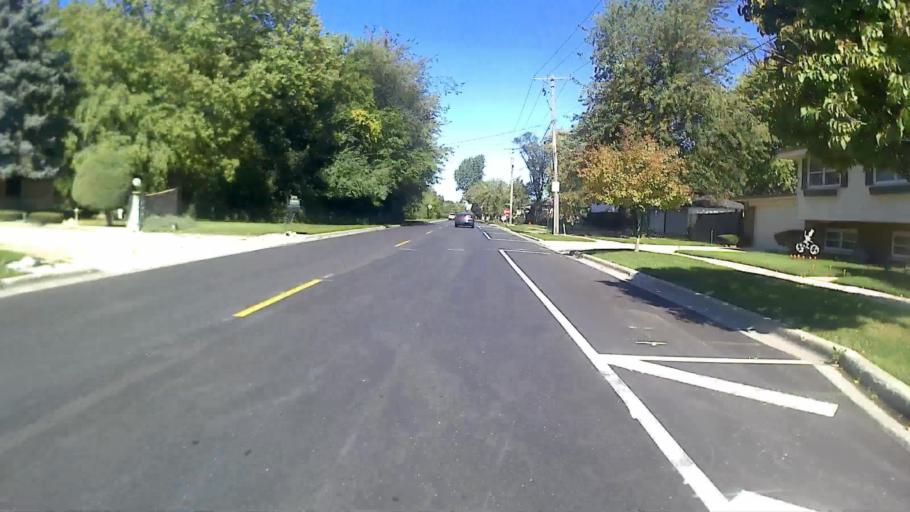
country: US
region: Illinois
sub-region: DuPage County
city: Itasca
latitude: 41.9528
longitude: -88.0033
